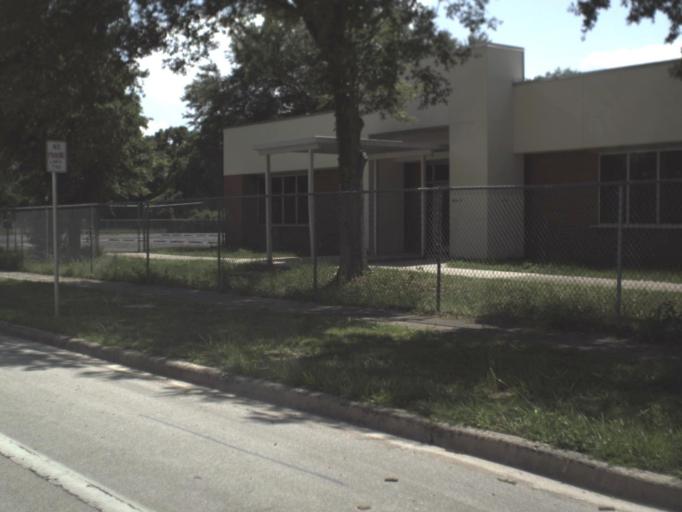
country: US
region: Florida
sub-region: Gilchrist County
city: Trenton
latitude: 29.6190
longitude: -82.8185
